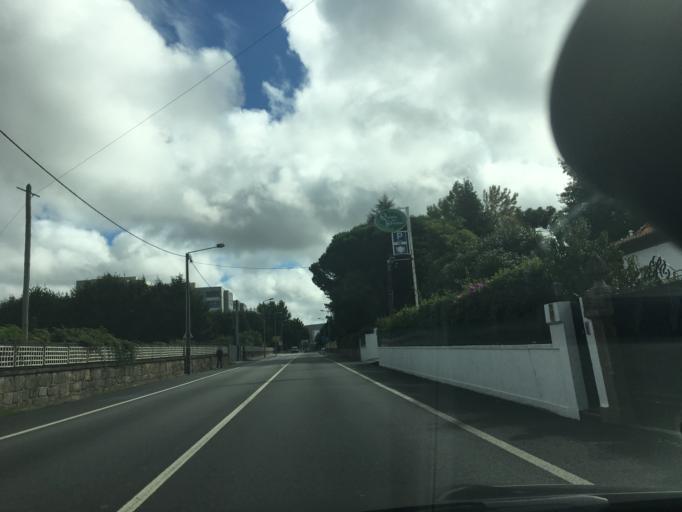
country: PT
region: Porto
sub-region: Maia
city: Gemunde
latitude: 41.2578
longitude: -8.6573
